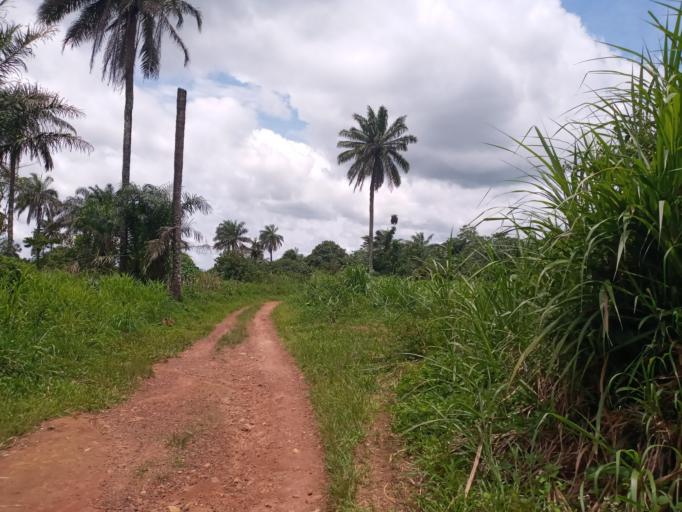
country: SL
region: Eastern Province
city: Koidu
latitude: 8.6445
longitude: -10.9090
